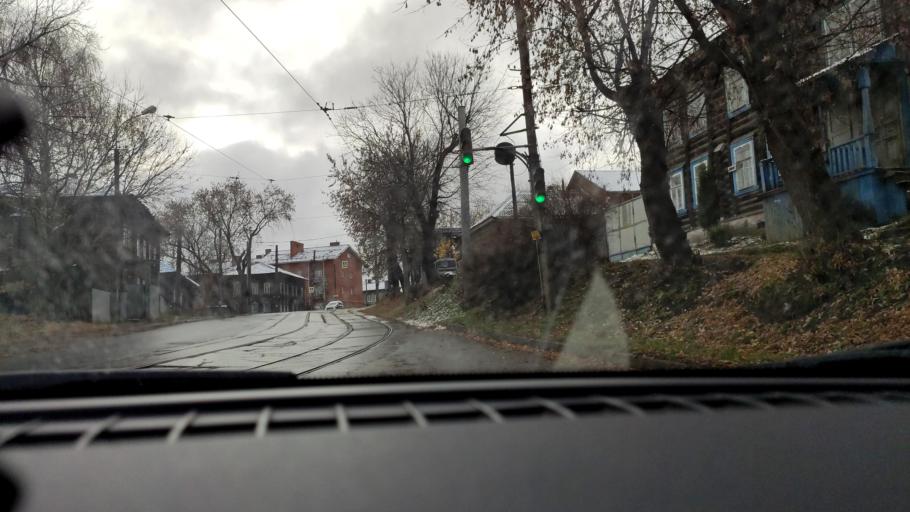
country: RU
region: Perm
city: Perm
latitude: 58.0348
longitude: 56.3118
